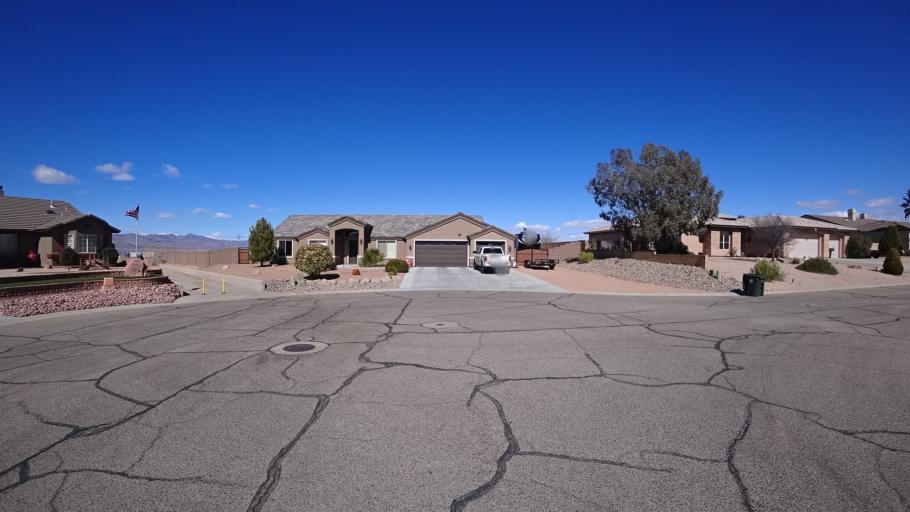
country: US
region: Arizona
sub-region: Mohave County
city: New Kingman-Butler
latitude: 35.2098
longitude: -113.9753
